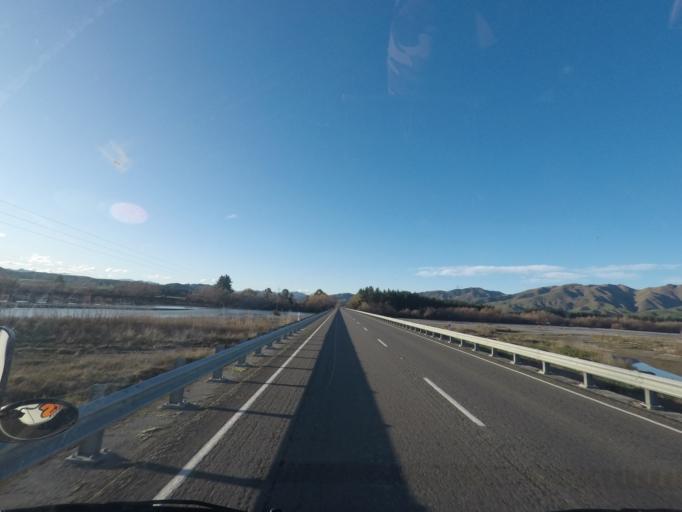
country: NZ
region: Canterbury
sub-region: Kaikoura District
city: Kaikoura
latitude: -42.7226
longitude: 173.2832
